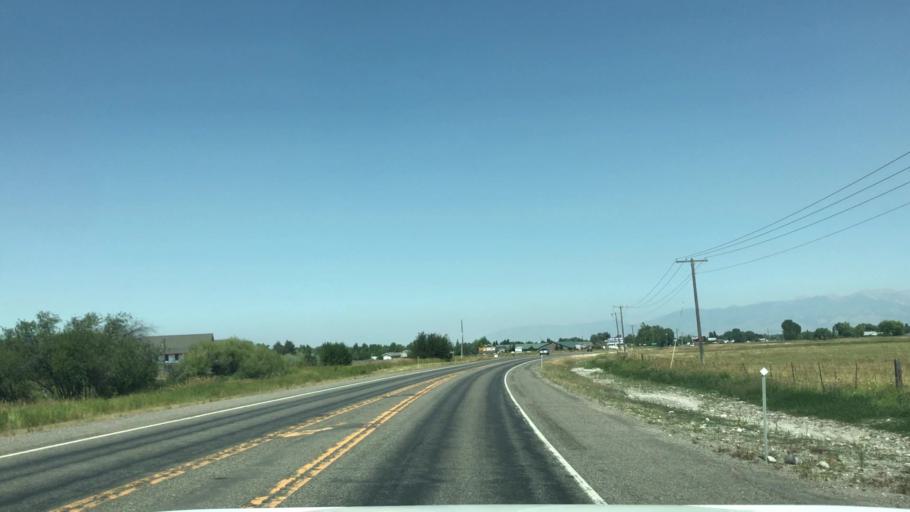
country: US
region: Montana
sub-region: Gallatin County
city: Four Corners
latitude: 45.6409
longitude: -111.1965
